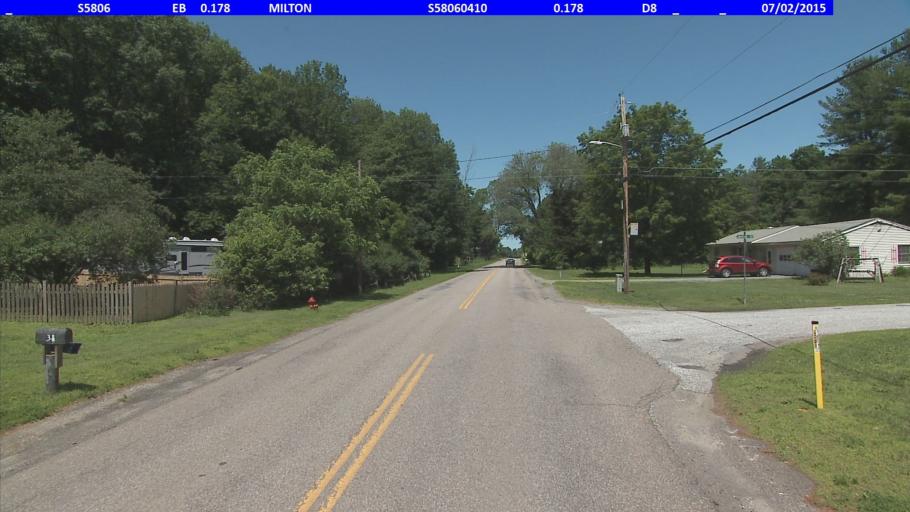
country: US
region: Vermont
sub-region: Chittenden County
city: Milton
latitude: 44.6537
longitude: -73.1170
